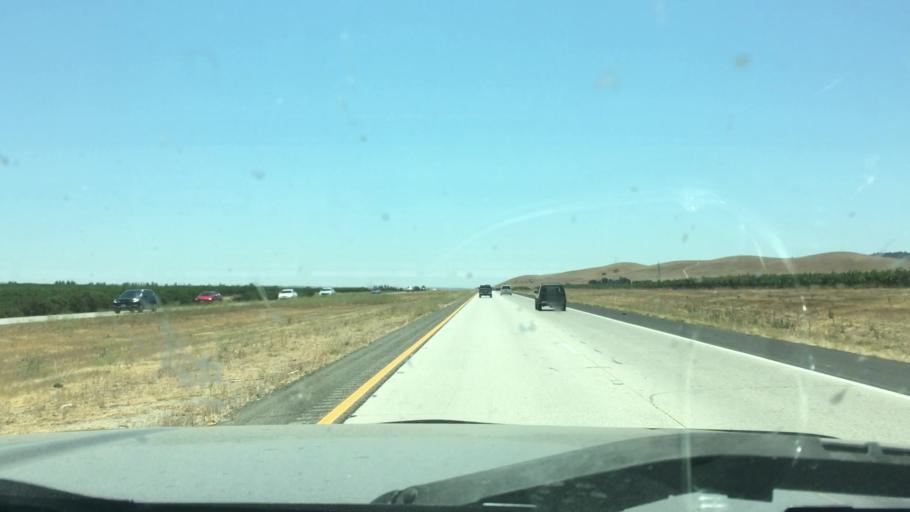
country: US
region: California
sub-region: Monterey County
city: King City
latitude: 36.0647
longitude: -120.9833
